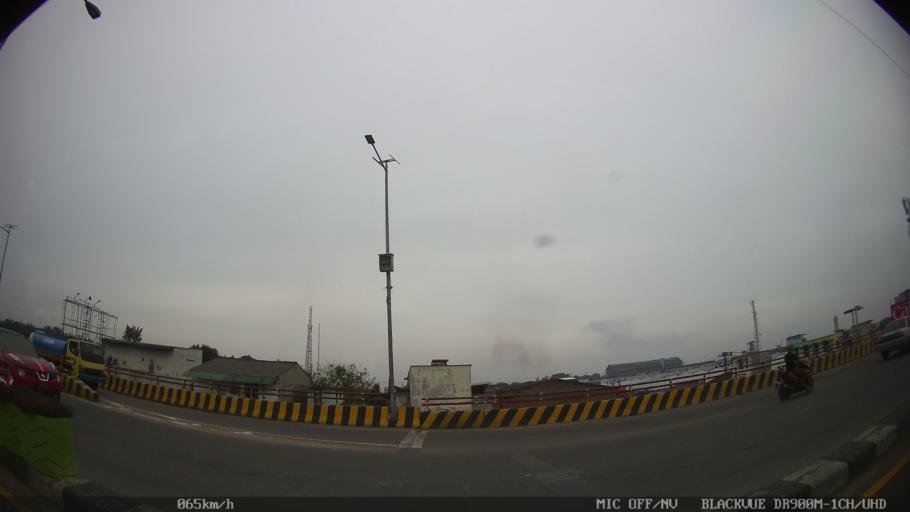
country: ID
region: North Sumatra
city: Deli Tua
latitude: 3.5365
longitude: 98.7168
